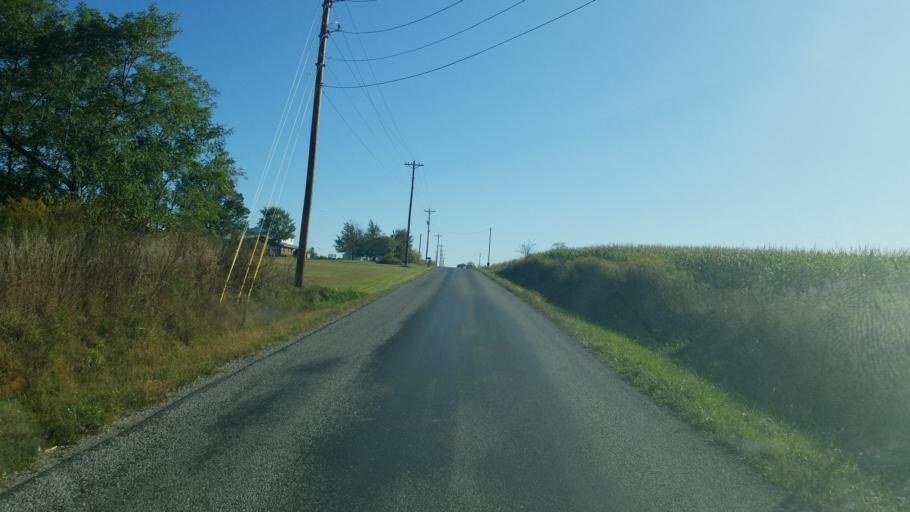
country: US
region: Ohio
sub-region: Wayne County
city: Creston
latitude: 40.9358
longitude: -81.9756
